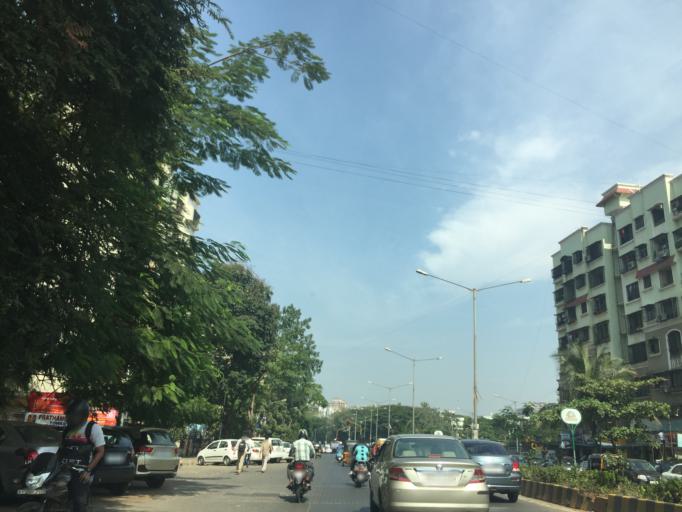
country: IN
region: Maharashtra
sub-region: Mumbai Suburban
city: Borivli
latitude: 19.2283
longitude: 72.8408
